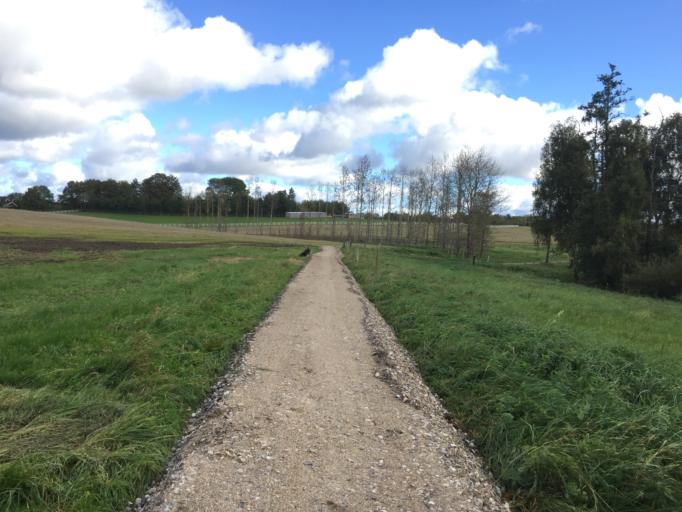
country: DK
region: Zealand
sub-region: Koge Kommune
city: Borup
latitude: 55.4786
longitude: 11.8873
